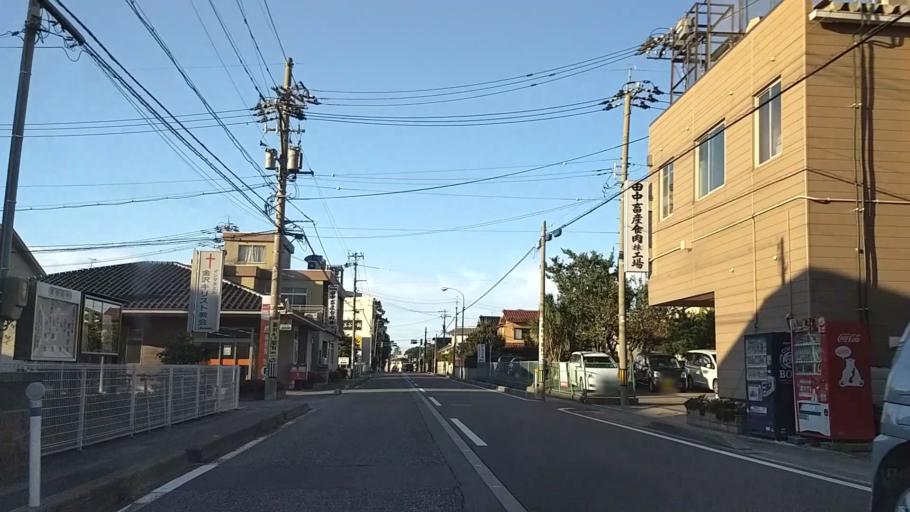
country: JP
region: Ishikawa
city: Nonoichi
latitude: 36.5483
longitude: 136.6493
